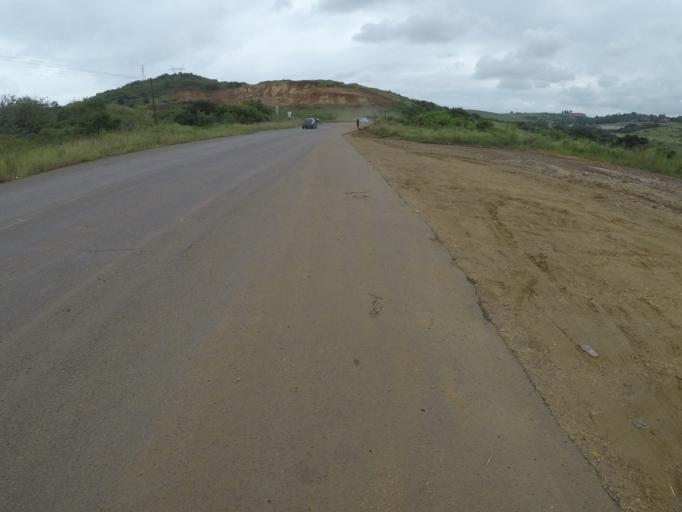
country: ZA
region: KwaZulu-Natal
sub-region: uThungulu District Municipality
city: Empangeni
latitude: -28.7569
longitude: 31.8742
